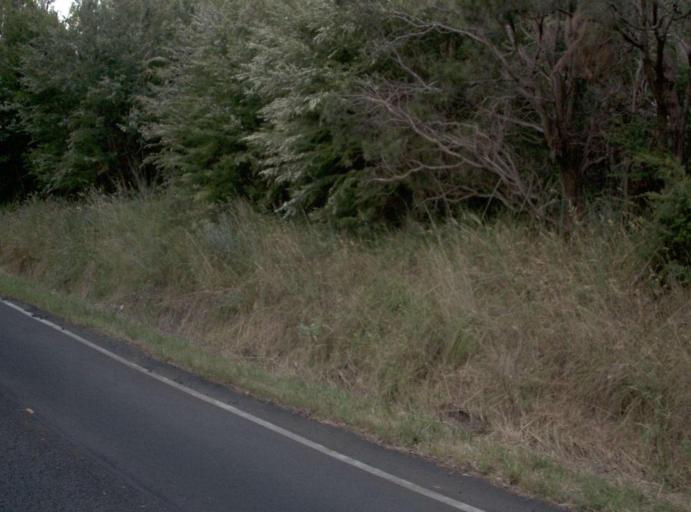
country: AU
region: Victoria
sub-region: Latrobe
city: Morwell
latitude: -38.2005
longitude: 146.4018
